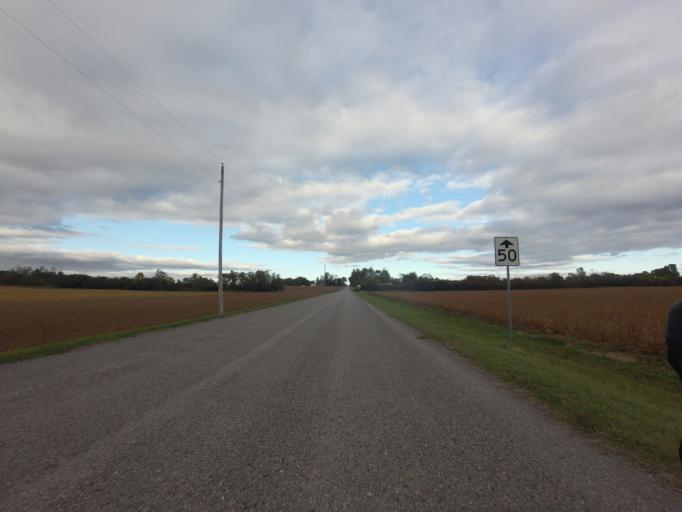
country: CA
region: Ontario
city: Cobourg
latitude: 43.9830
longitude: -77.9125
